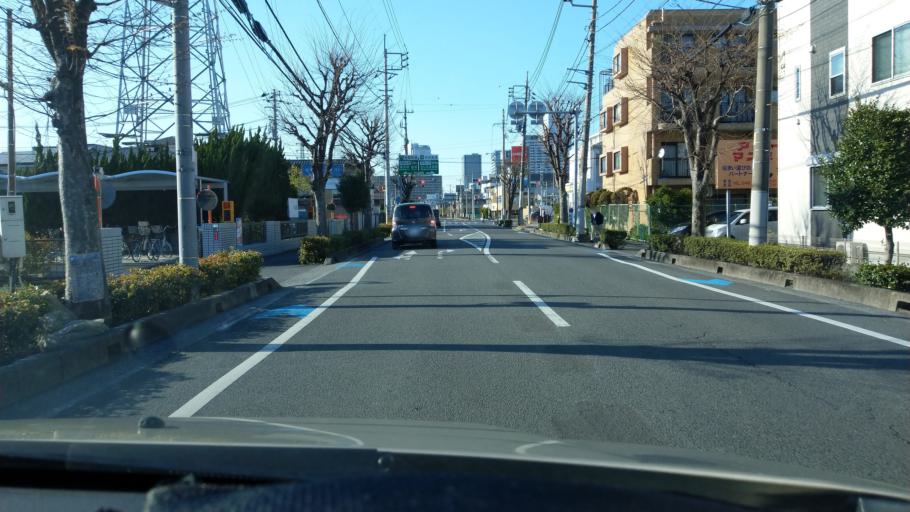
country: JP
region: Saitama
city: Yono
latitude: 35.8959
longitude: 139.6216
